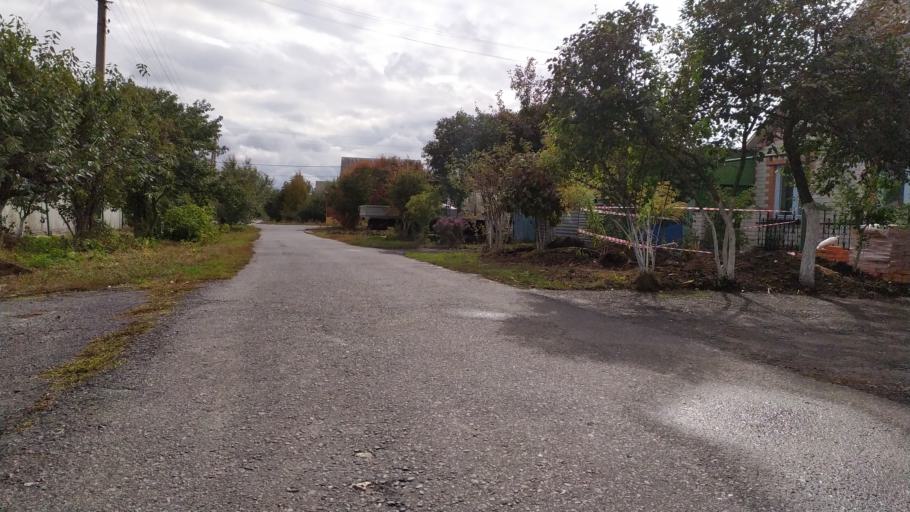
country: RU
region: Kursk
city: Kursk
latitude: 51.6446
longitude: 36.1531
